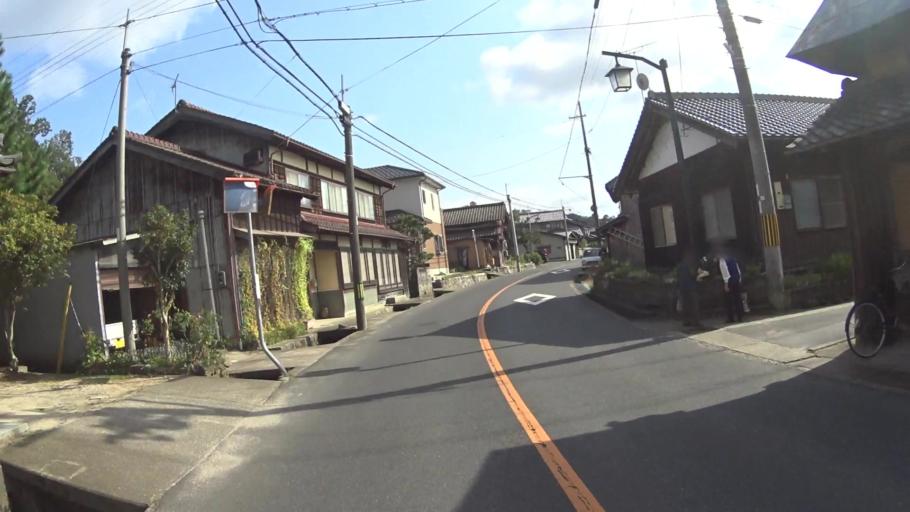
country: JP
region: Kyoto
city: Miyazu
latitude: 35.5884
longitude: 135.1019
